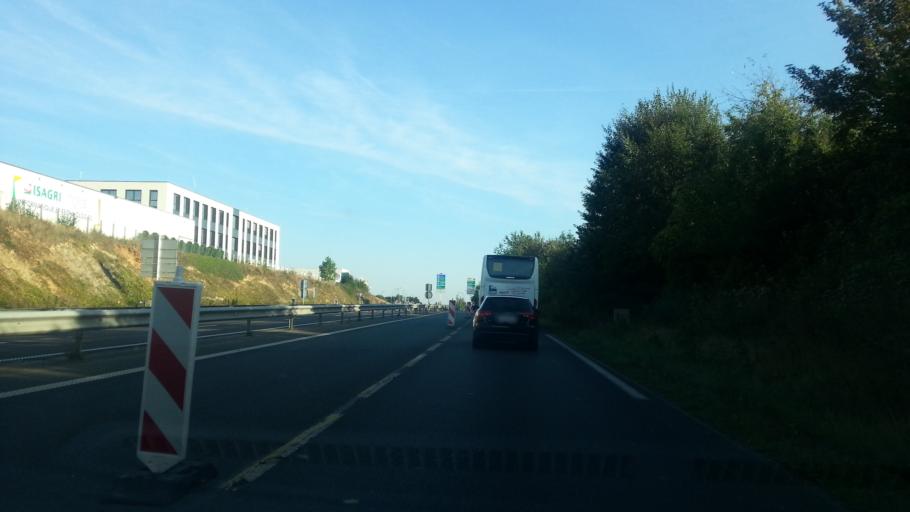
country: FR
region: Picardie
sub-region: Departement de l'Oise
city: Tille
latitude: 49.4555
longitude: 2.0939
